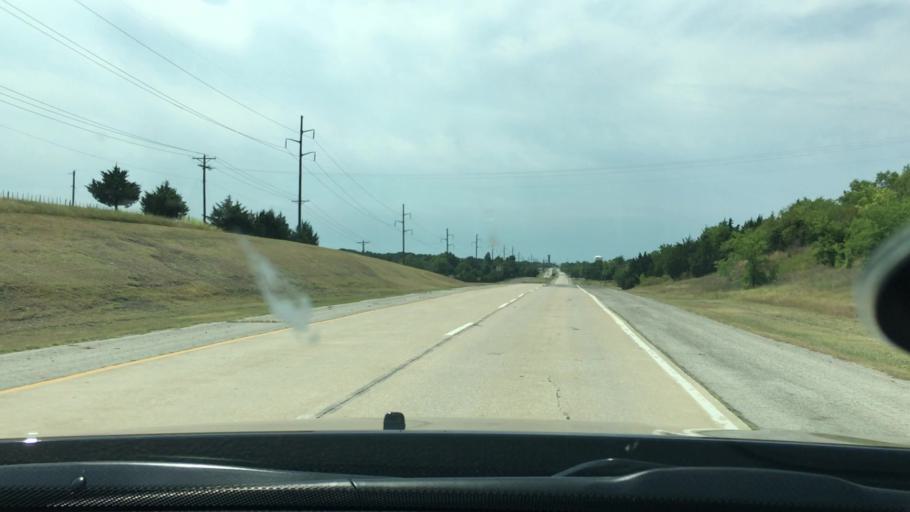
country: US
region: Oklahoma
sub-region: Carter County
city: Ardmore
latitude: 34.2270
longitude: -97.1433
